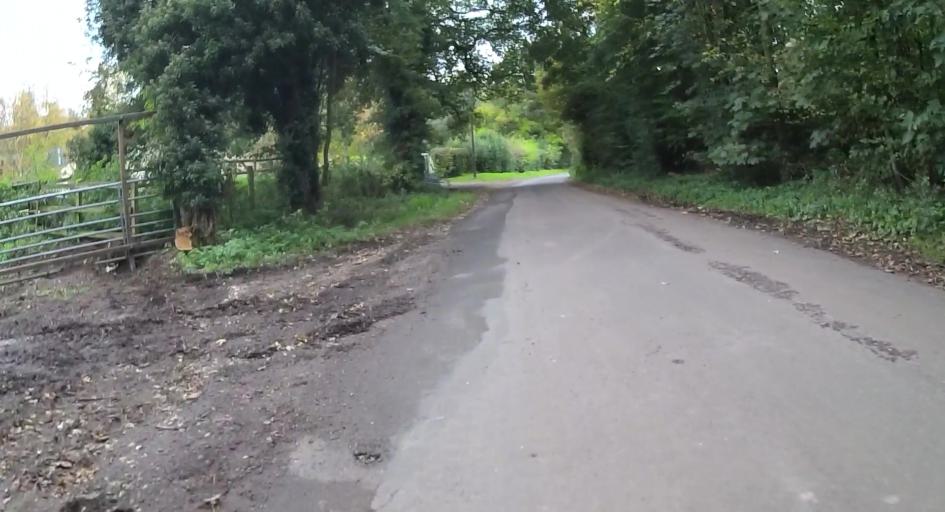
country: GB
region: England
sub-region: Hampshire
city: Four Marks
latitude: 51.1070
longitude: -1.0680
